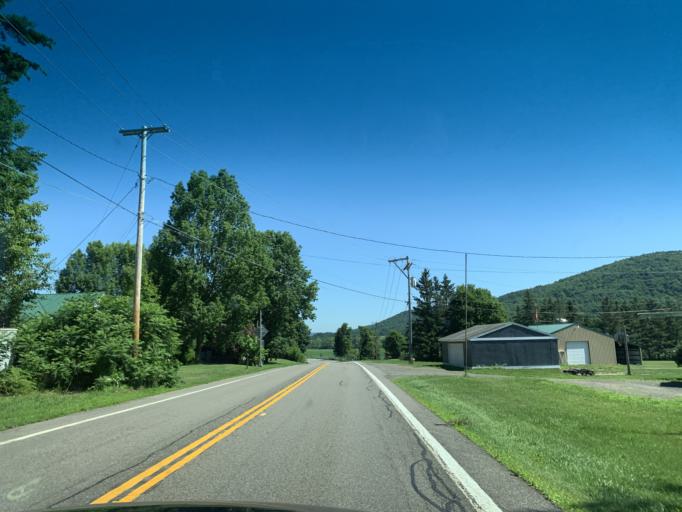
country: US
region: New York
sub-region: Chenango County
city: Norwich
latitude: 42.4870
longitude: -75.4027
